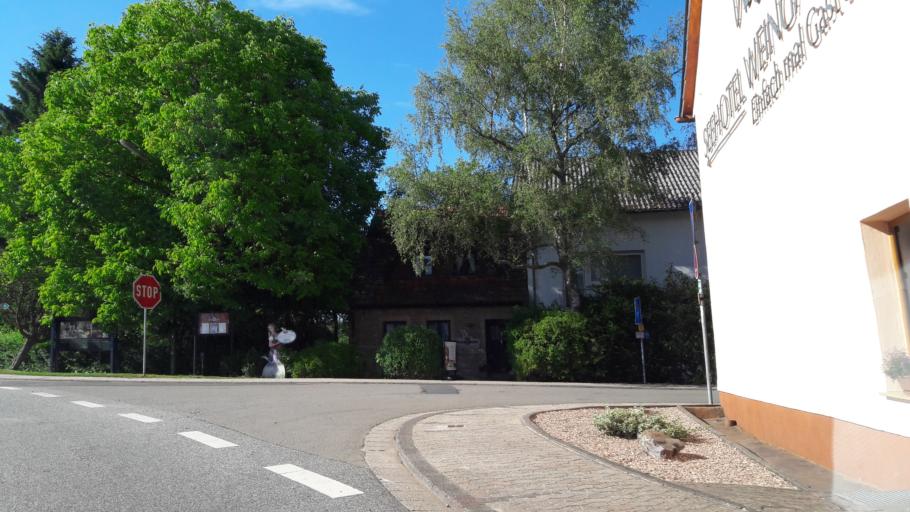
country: DE
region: Rheinland-Pfalz
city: Achtelsbach
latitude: 49.5684
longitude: 7.0586
